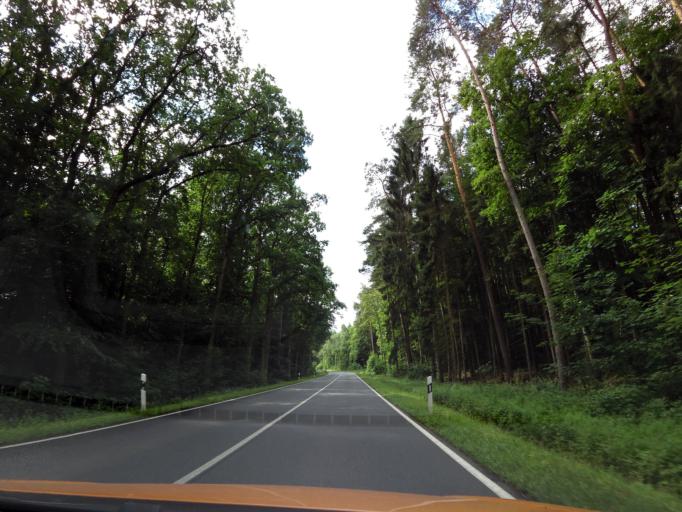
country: DE
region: Mecklenburg-Vorpommern
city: Krakow am See
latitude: 53.5982
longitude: 12.2590
